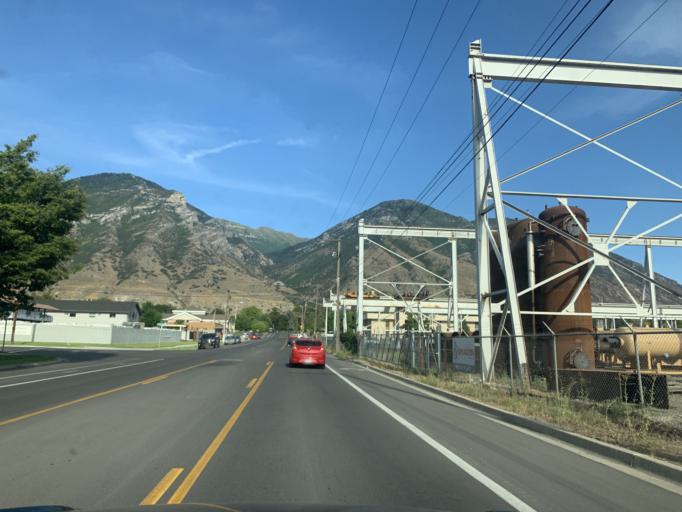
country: US
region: Utah
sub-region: Utah County
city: Provo
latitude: 40.2256
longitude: -111.6505
